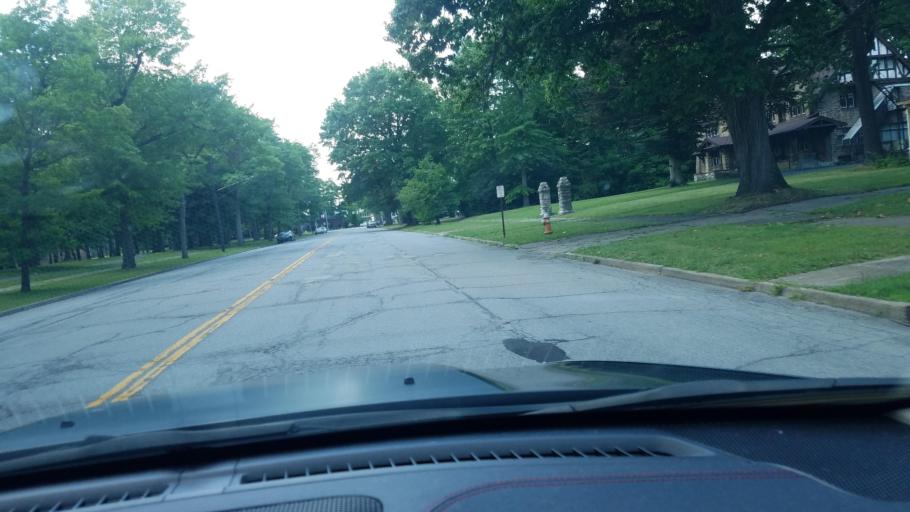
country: US
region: Ohio
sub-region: Mahoning County
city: Youngstown
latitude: 41.1165
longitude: -80.6481
